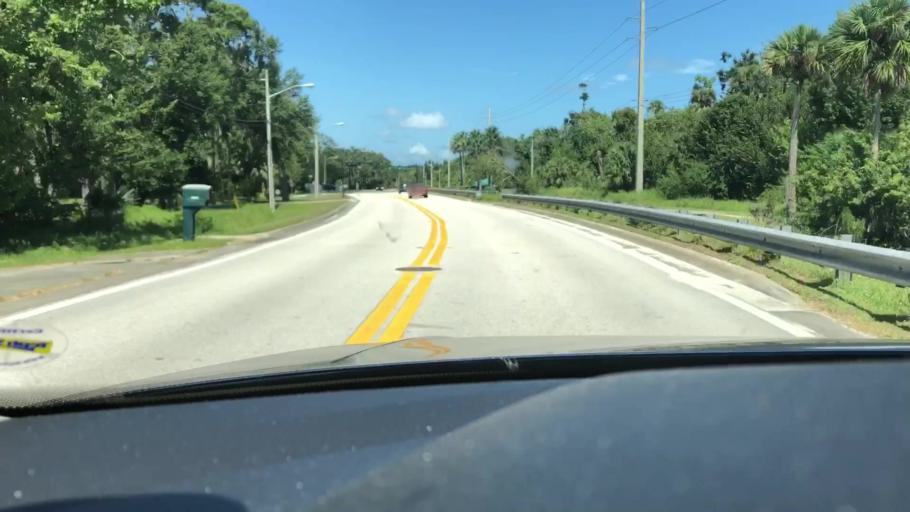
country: US
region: Florida
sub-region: Volusia County
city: Port Orange
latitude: 29.1296
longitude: -80.9931
